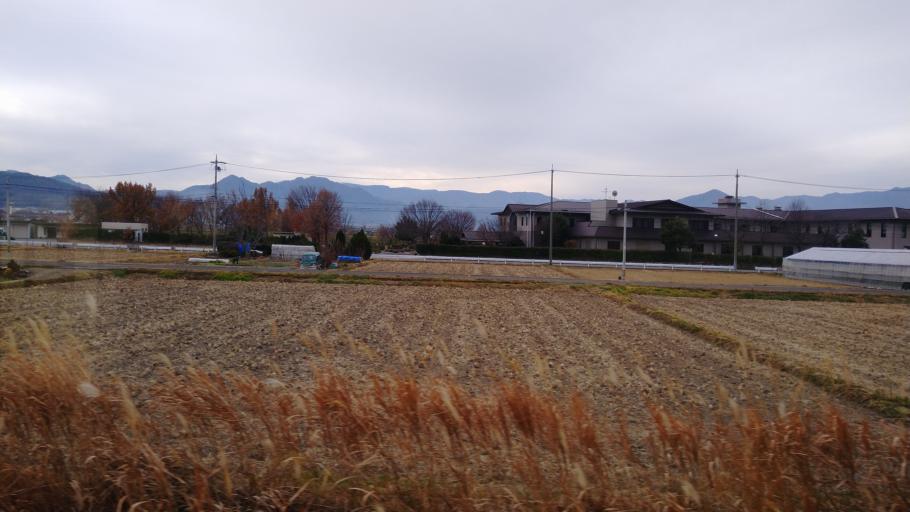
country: JP
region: Nagano
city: Ueda
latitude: 36.4092
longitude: 138.2289
